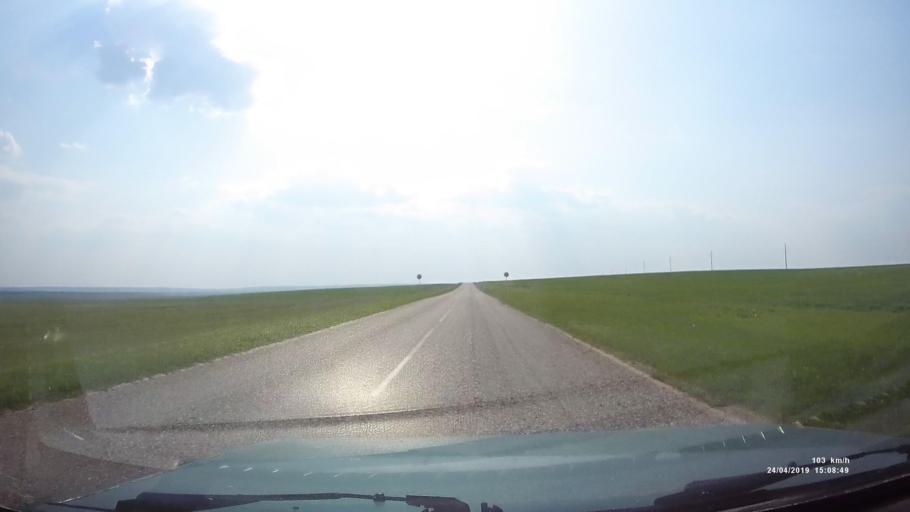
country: RU
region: Rostov
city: Remontnoye
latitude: 46.5581
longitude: 43.3748
